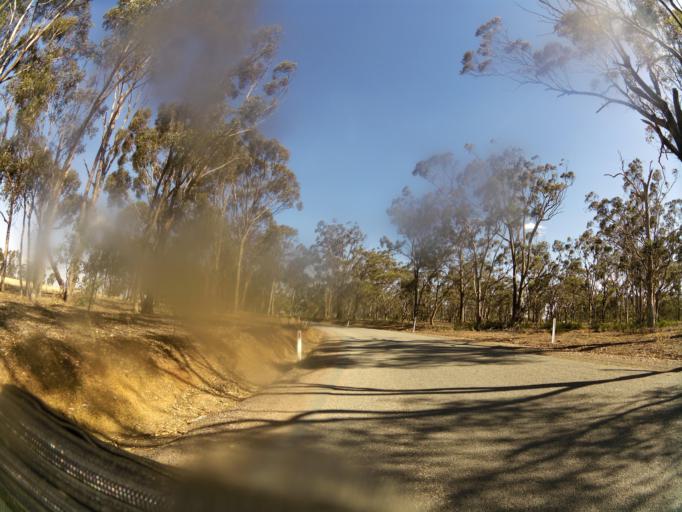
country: AU
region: Victoria
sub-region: Campaspe
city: Kyabram
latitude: -36.8770
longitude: 145.0855
